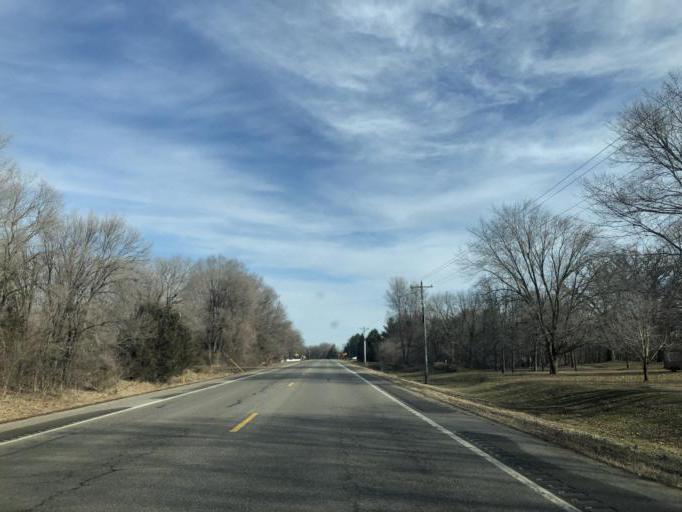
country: US
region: Minnesota
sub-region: Sherburne County
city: Becker
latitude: 45.4154
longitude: -93.8709
